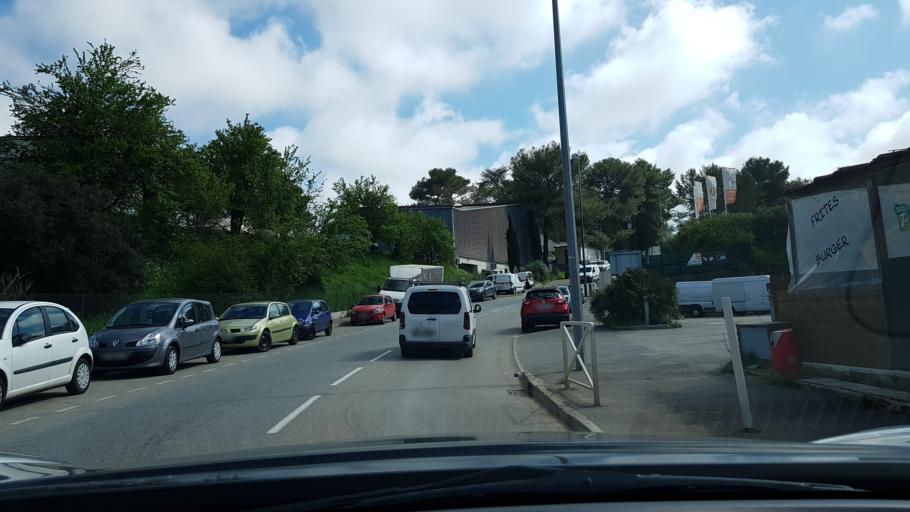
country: FR
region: Provence-Alpes-Cote d'Azur
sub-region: Departement des Alpes-Maritimes
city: Biot
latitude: 43.6047
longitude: 7.0769
